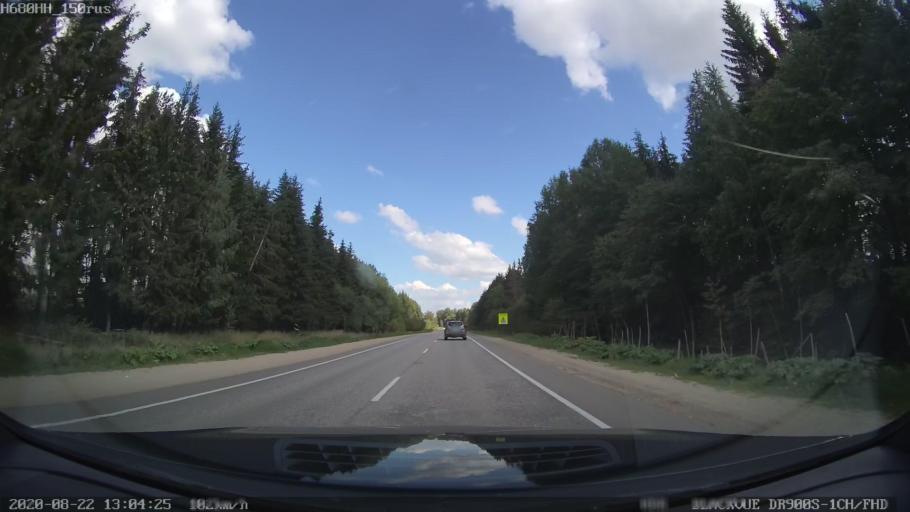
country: RU
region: Tverskaya
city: Bezhetsk
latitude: 57.6662
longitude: 36.4305
